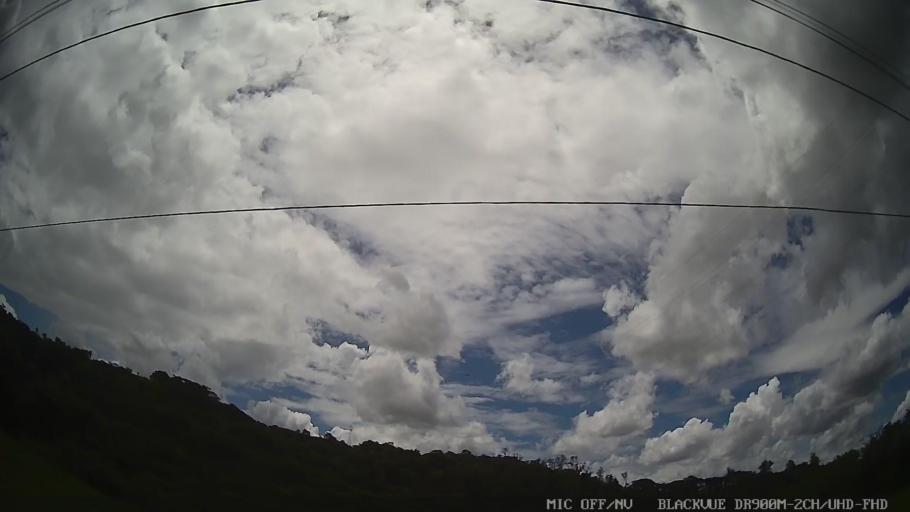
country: BR
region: Sao Paulo
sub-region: Jaguariuna
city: Jaguariuna
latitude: -22.6944
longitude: -46.9593
